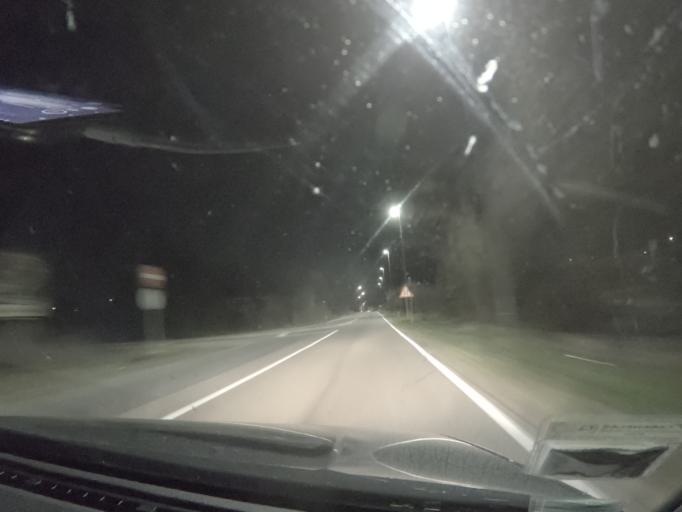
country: ES
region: Castille and Leon
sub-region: Provincia de Zamora
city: Benavente
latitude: 42.0120
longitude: -5.6674
